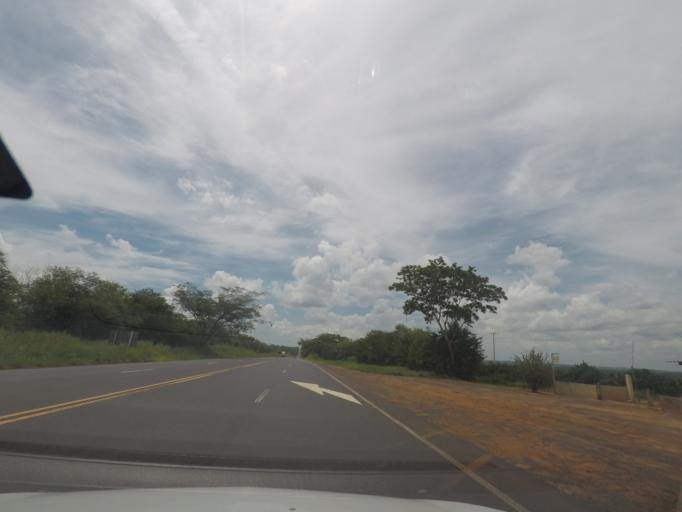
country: BR
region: Sao Paulo
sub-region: Barretos
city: Barretos
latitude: -20.4179
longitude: -48.6315
